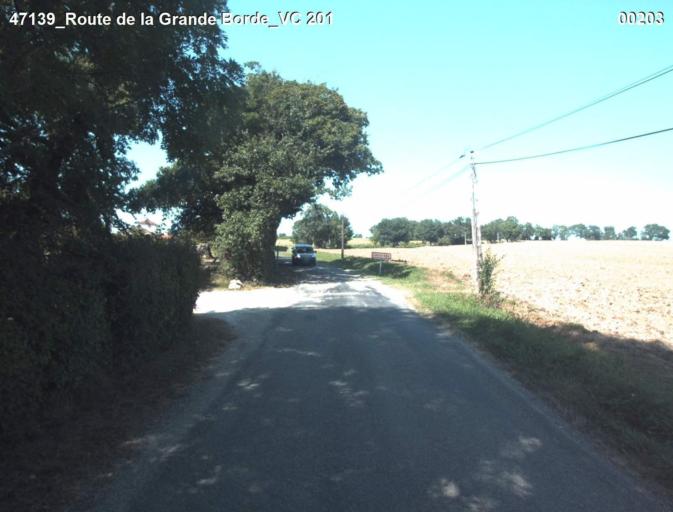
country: FR
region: Aquitaine
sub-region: Departement du Lot-et-Garonne
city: Nerac
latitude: 44.0639
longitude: 0.3933
